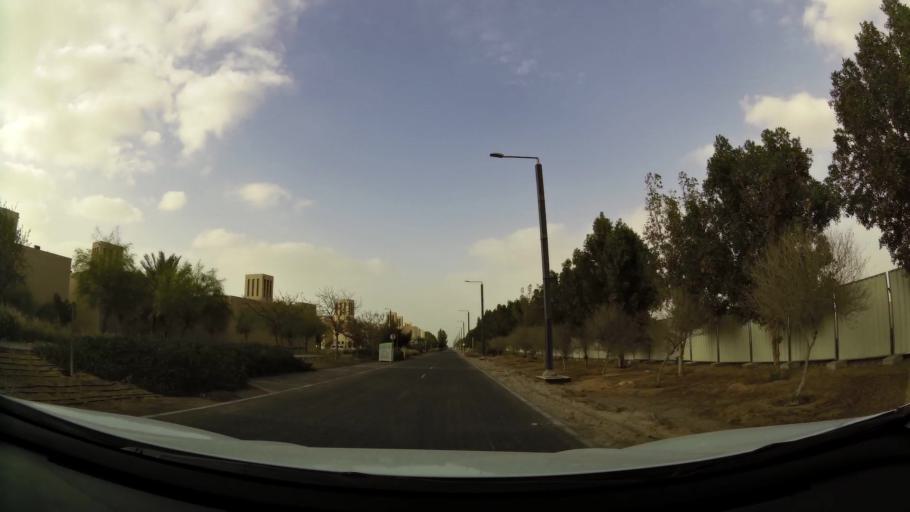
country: AE
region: Abu Dhabi
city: Abu Dhabi
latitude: 24.5048
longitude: 54.6025
